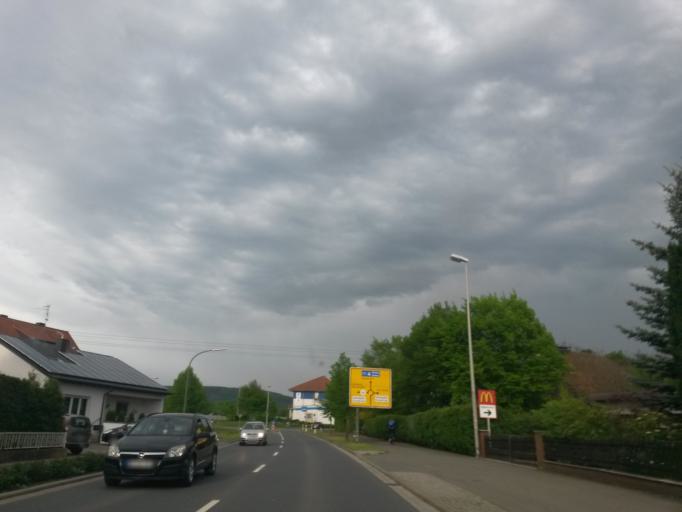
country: DE
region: Bavaria
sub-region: Upper Franconia
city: Hirschaid
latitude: 49.8203
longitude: 10.9977
